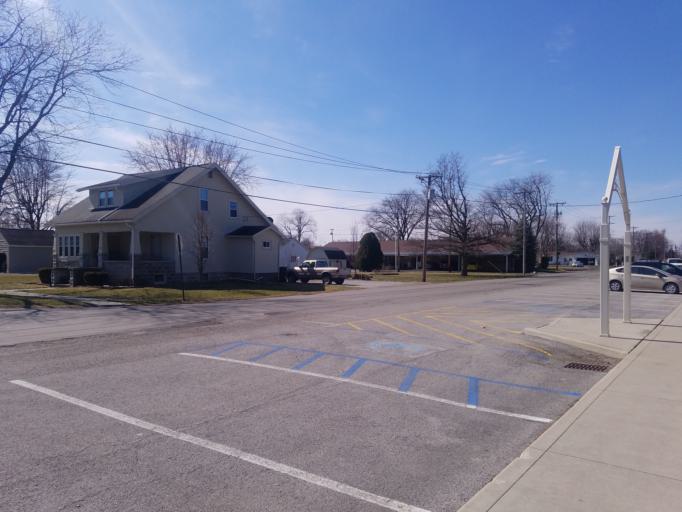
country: US
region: Ohio
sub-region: Allen County
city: Delphos
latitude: 40.8526
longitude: -84.3411
